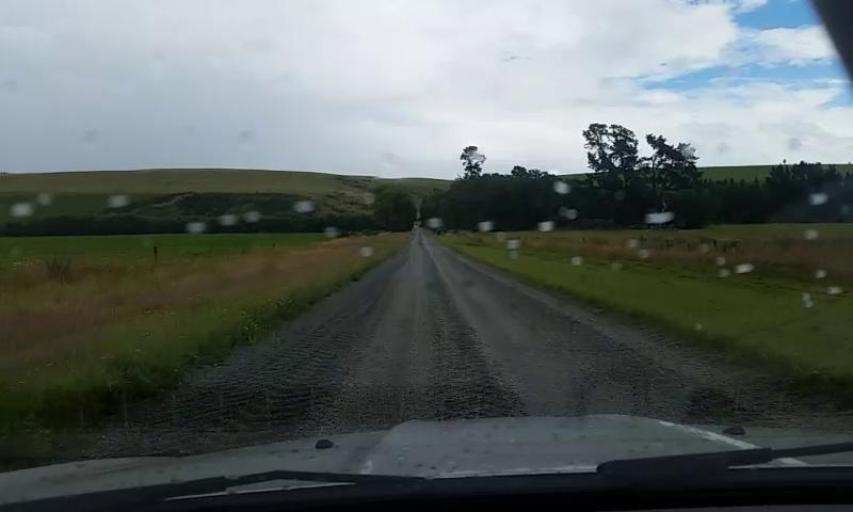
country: NZ
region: Canterbury
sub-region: Ashburton District
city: Methven
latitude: -43.7184
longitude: 171.3623
